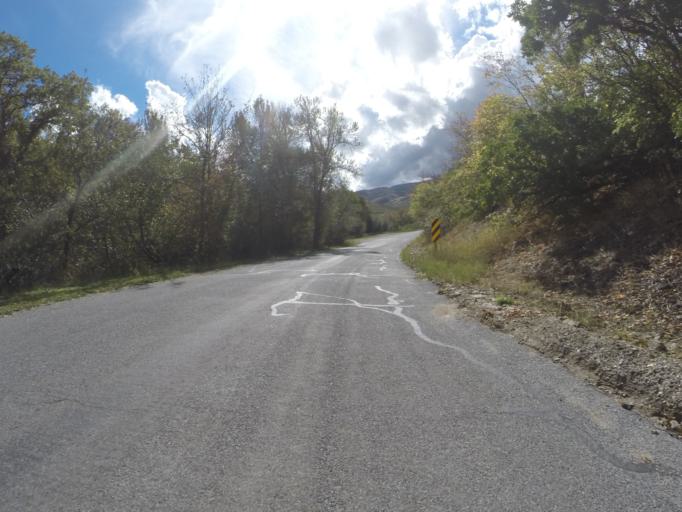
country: US
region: Utah
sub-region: Salt Lake County
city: Herriman
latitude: 40.4956
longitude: -112.1145
